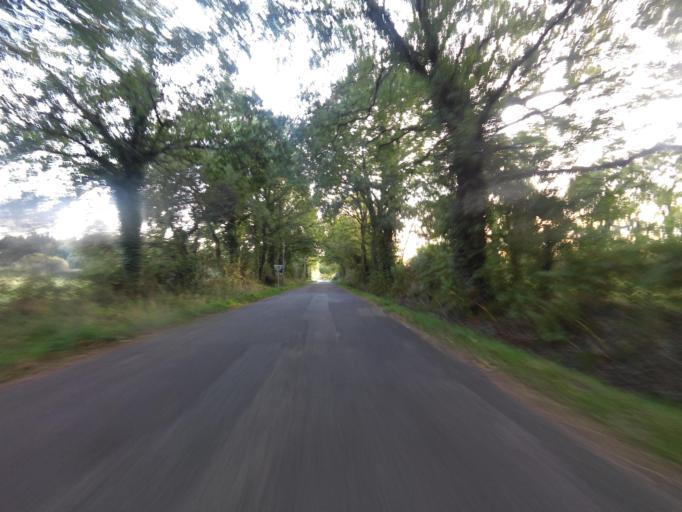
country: FR
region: Brittany
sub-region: Departement du Morbihan
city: Theix
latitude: 47.6383
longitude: -2.6876
